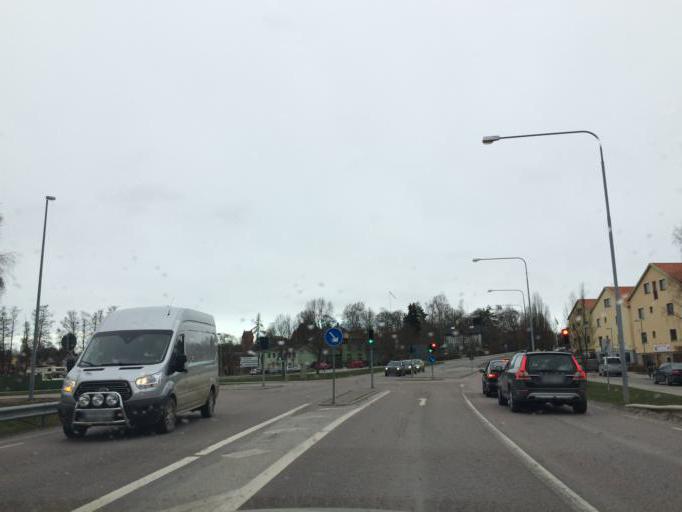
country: SE
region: Soedermanland
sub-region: Eskilstuna Kommun
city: Torshalla
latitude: 59.4171
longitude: 16.4734
